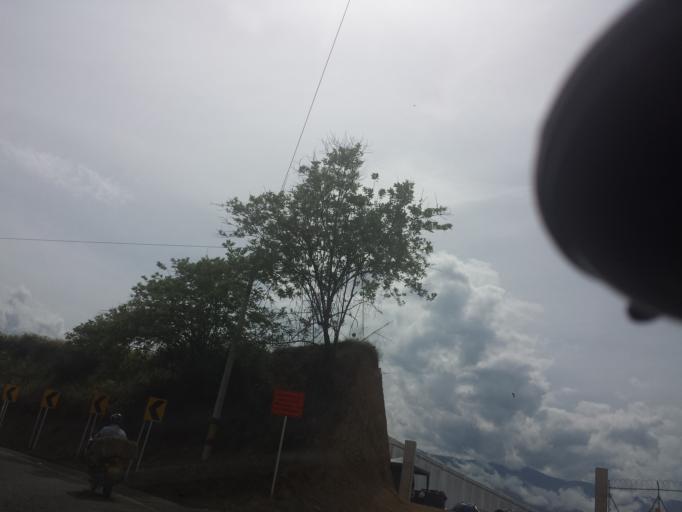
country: CO
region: Antioquia
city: Antioquia
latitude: 6.5685
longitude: -75.8374
